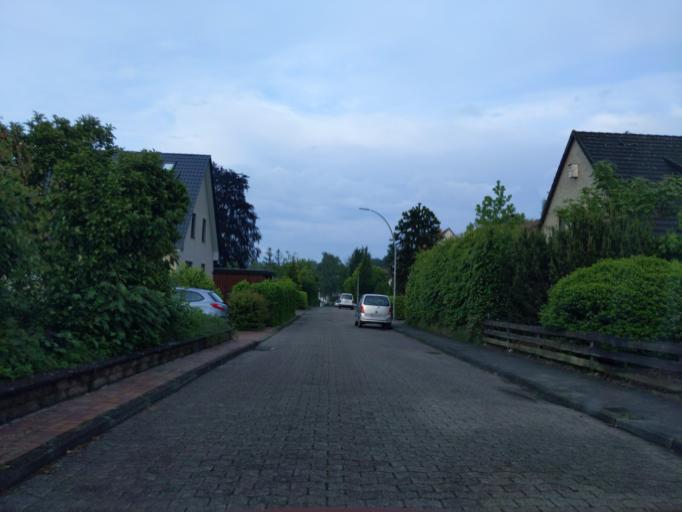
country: DE
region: Lower Saxony
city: Walsrode
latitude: 52.8708
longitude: 9.5905
